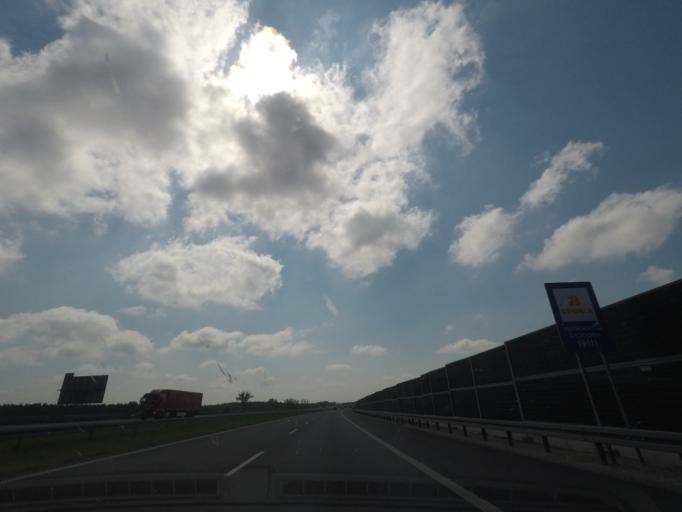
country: PL
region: Kujawsko-Pomorskie
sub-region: Powiat wloclawski
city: Brzesc Kujawski
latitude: 52.6053
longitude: 18.9819
